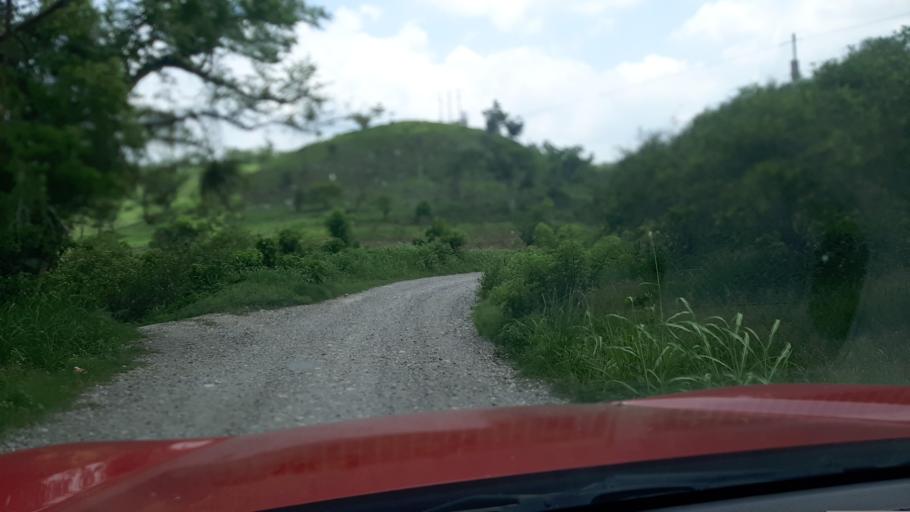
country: MX
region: Veracruz
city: Agua Dulce
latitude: 20.4135
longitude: -97.2781
